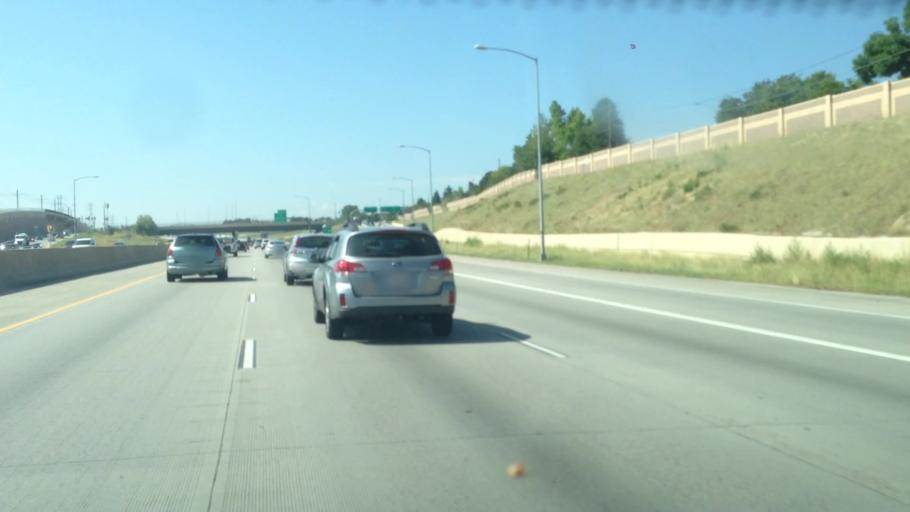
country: US
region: Colorado
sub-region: Adams County
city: Aurora
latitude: 39.7008
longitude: -104.8292
